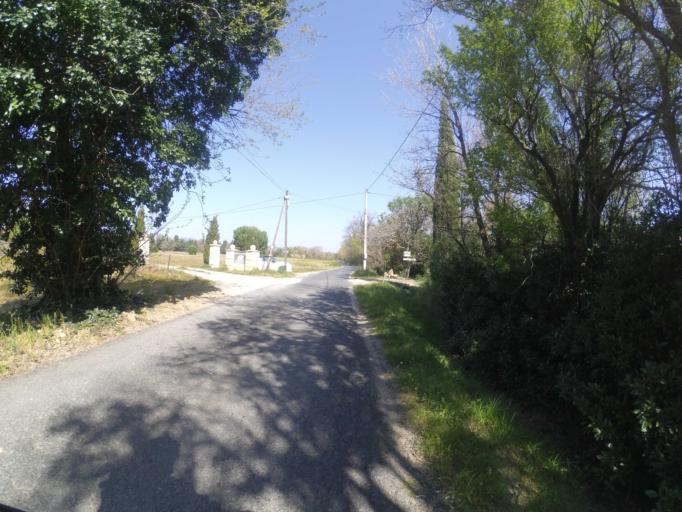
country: FR
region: Languedoc-Roussillon
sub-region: Departement des Pyrenees-Orientales
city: Thuir
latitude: 42.6578
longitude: 2.7598
